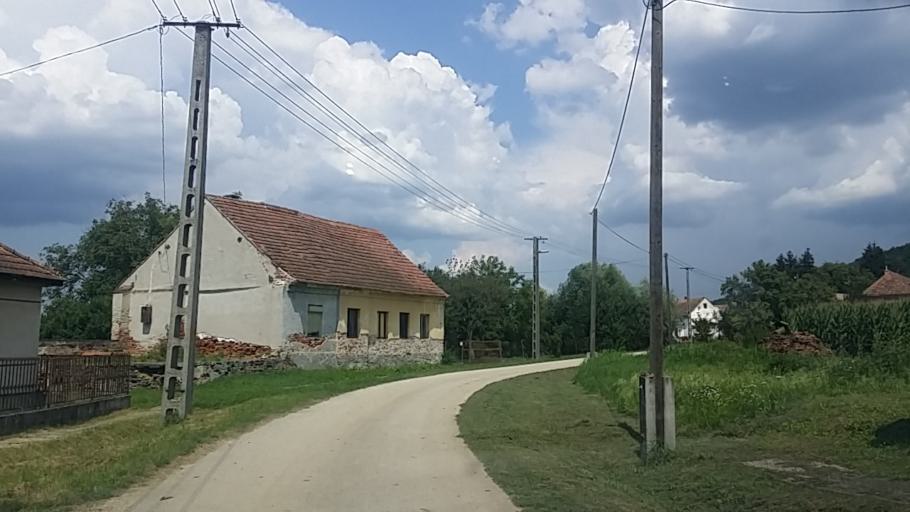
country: HR
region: Medimurska
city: Podturen
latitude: 46.5324
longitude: 16.5860
